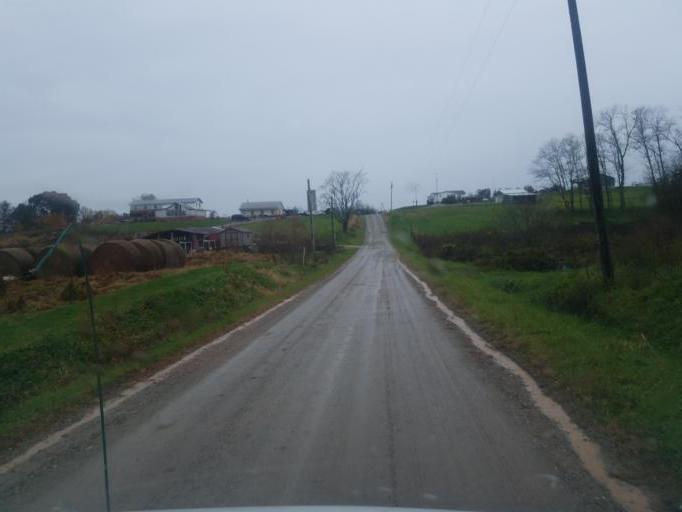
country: US
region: Ohio
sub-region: Washington County
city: Beverly
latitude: 39.4711
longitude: -81.6915
